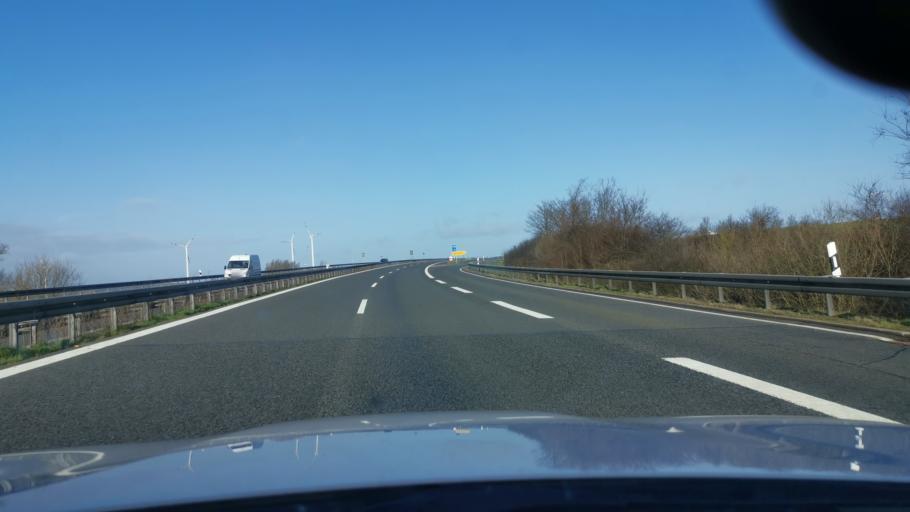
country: DE
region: Mecklenburg-Vorpommern
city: Stabelow
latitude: 54.0415
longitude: 12.0377
